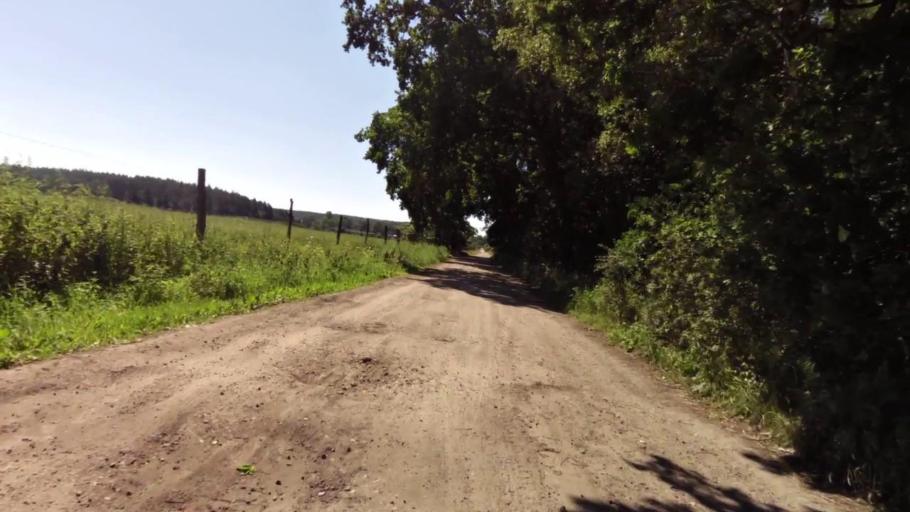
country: PL
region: West Pomeranian Voivodeship
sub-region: Powiat swidwinski
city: Rabino
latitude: 53.8945
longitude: 16.0097
